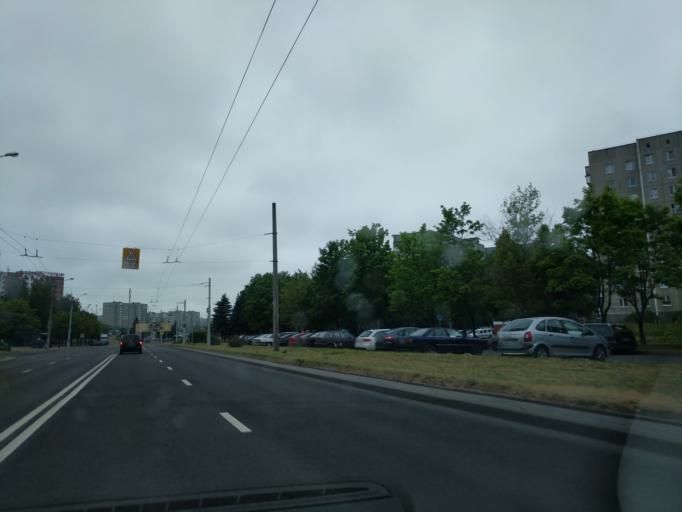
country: BY
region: Minsk
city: Novoye Medvezhino
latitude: 53.8640
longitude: 27.4676
